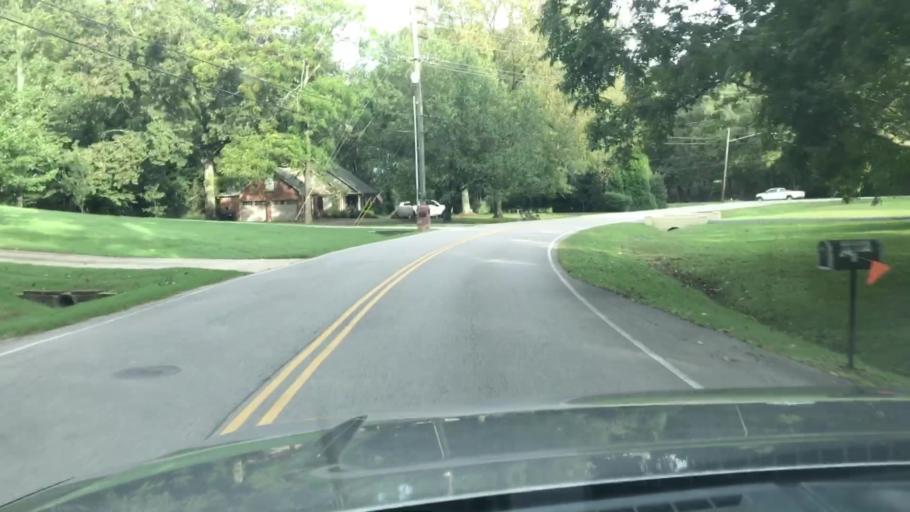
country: US
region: Tennessee
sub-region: Davidson County
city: Forest Hills
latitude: 36.0697
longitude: -86.8286
